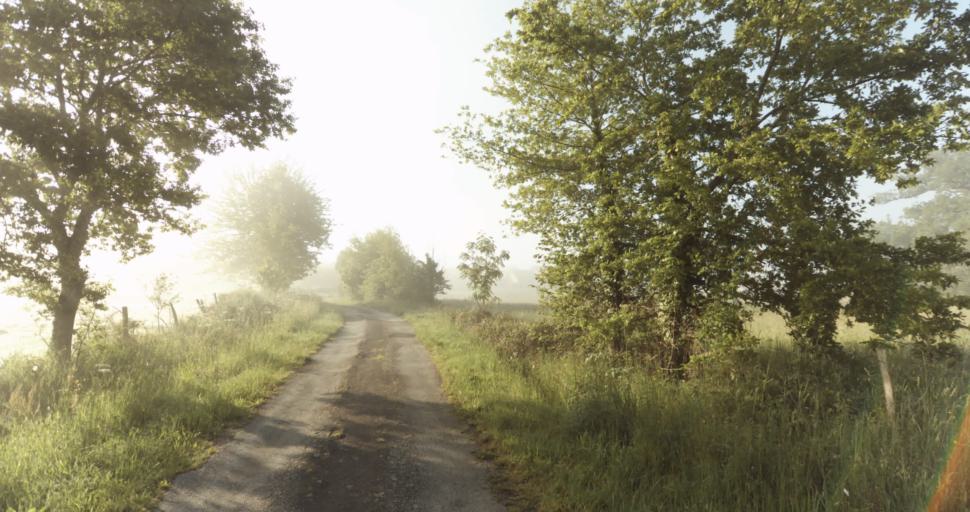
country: FR
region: Limousin
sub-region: Departement de la Haute-Vienne
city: Condat-sur-Vienne
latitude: 45.7858
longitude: 1.2813
